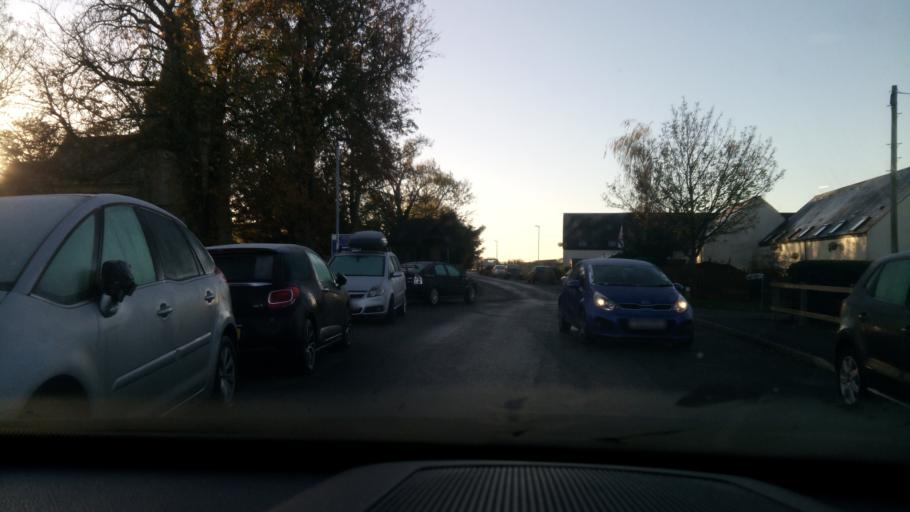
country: GB
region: England
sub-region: Peterborough
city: Wittering
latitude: 52.6061
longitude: -0.4424
